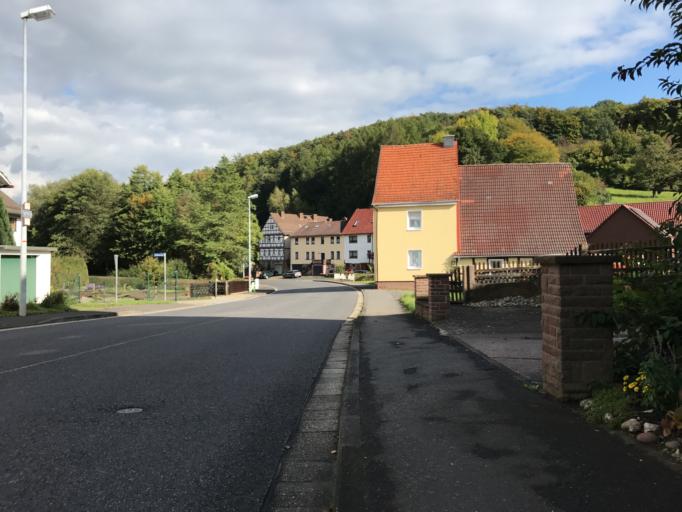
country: DE
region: Hesse
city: Witzenhausen
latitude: 51.3108
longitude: 9.8361
